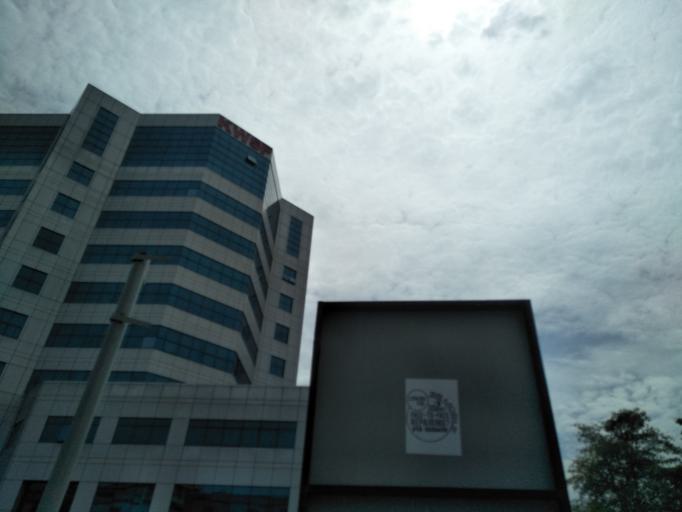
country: MY
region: Perak
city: Ipoh
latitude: 4.6027
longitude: 101.0931
